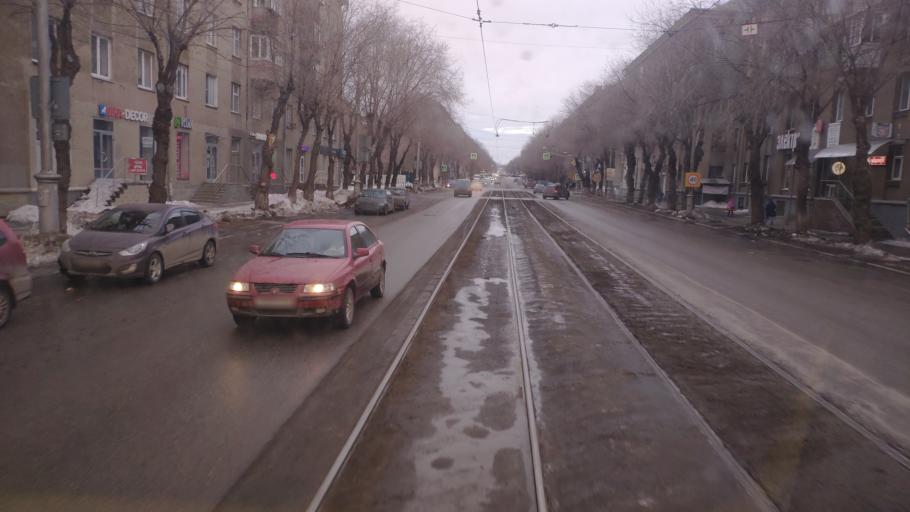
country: RU
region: Chelyabinsk
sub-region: Gorod Magnitogorsk
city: Magnitogorsk
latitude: 53.4178
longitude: 58.9901
